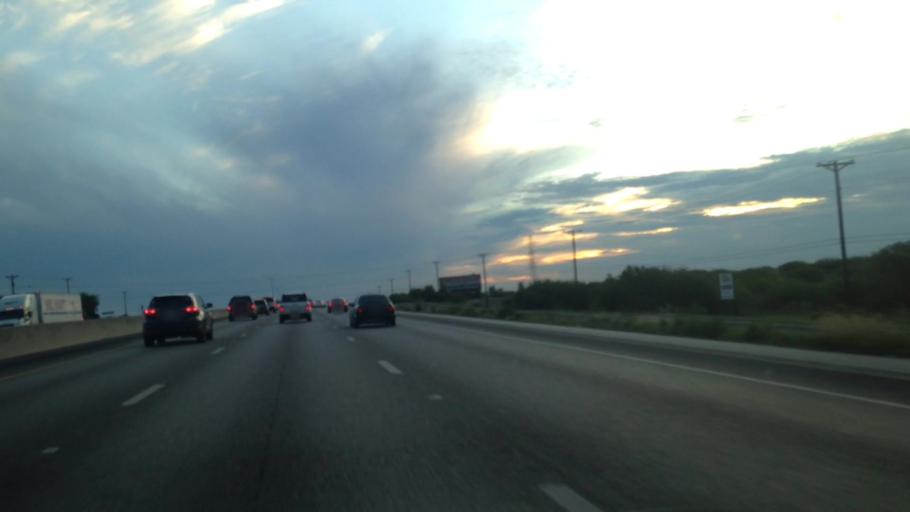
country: US
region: Texas
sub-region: Guadalupe County
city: Northcliff
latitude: 29.6456
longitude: -98.2019
